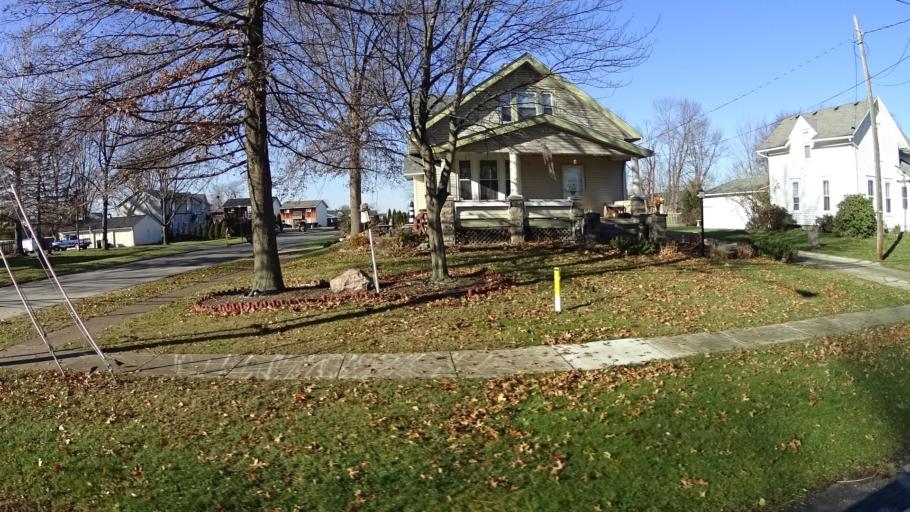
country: US
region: Ohio
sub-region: Lorain County
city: Lagrange
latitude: 41.2442
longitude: -82.1198
